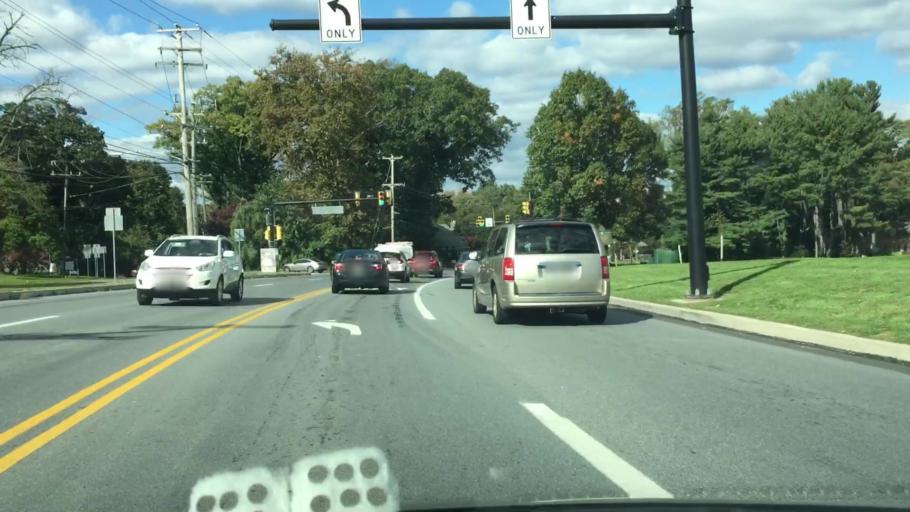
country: US
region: Pennsylvania
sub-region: Delaware County
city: Media
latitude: 39.9420
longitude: -75.3964
